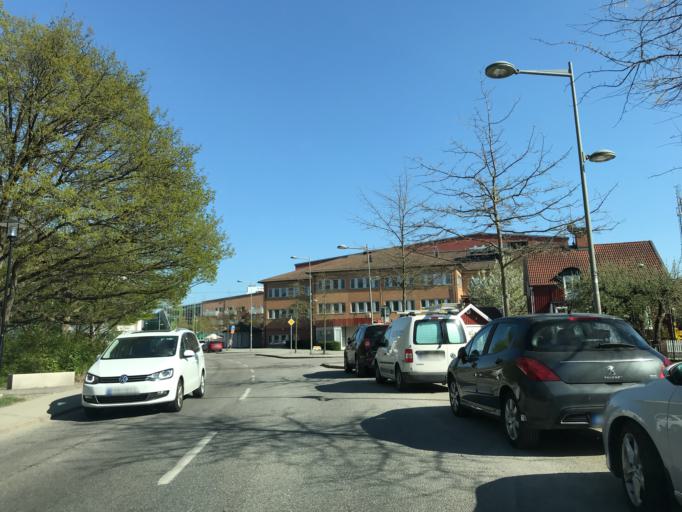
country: SE
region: Stockholm
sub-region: Stockholms Kommun
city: Arsta
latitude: 59.2795
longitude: 18.0062
